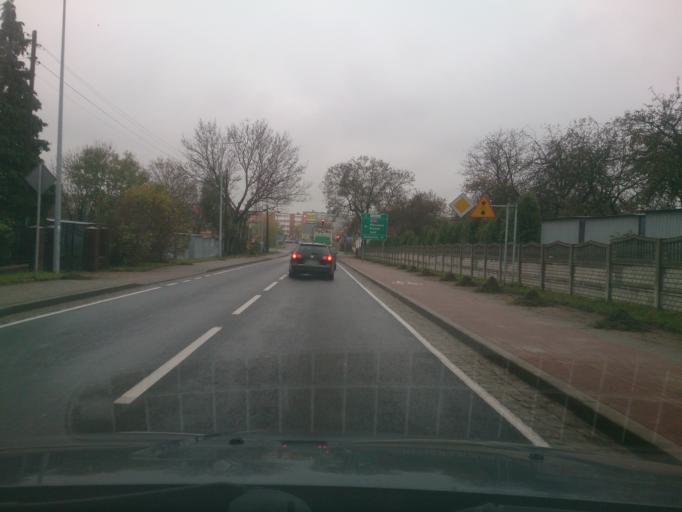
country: PL
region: Greater Poland Voivodeship
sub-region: Powiat kolski
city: Kolo
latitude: 52.2062
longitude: 18.6408
